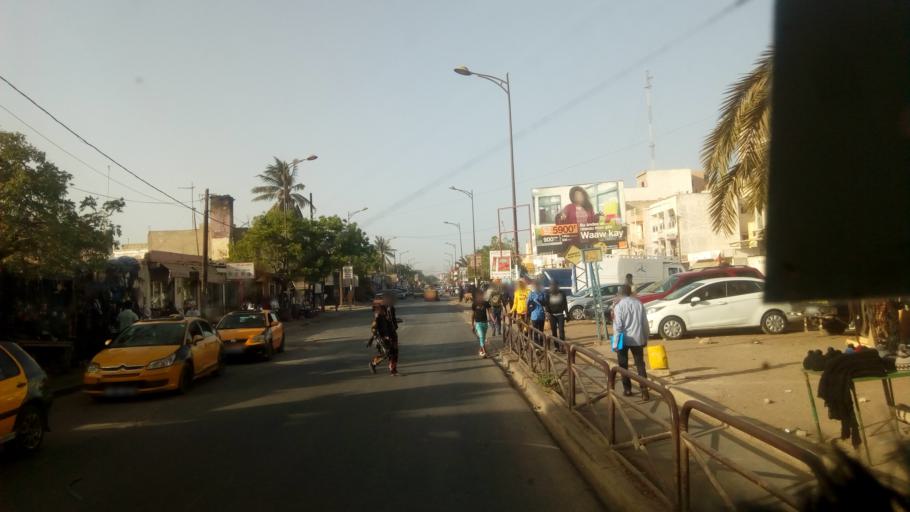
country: SN
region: Dakar
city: Dakar
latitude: 14.7023
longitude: -17.4470
